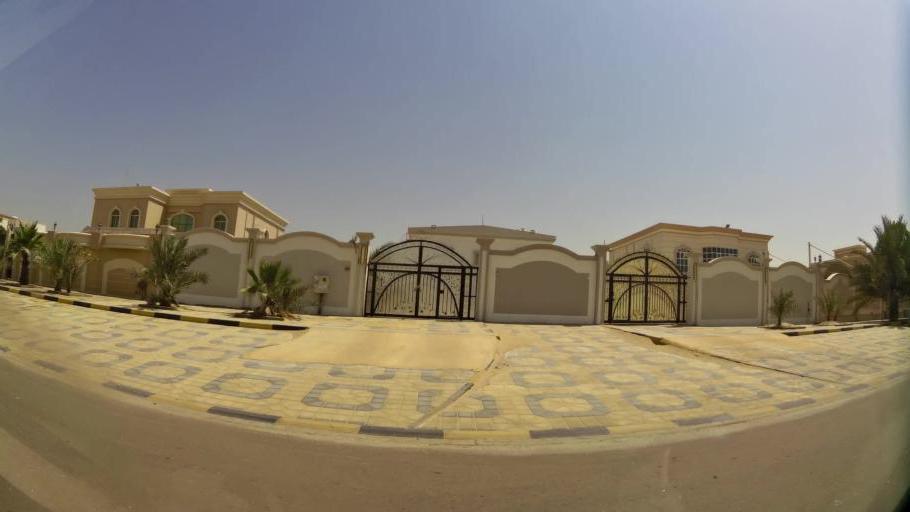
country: AE
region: Ajman
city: Ajman
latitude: 25.4195
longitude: 55.5241
